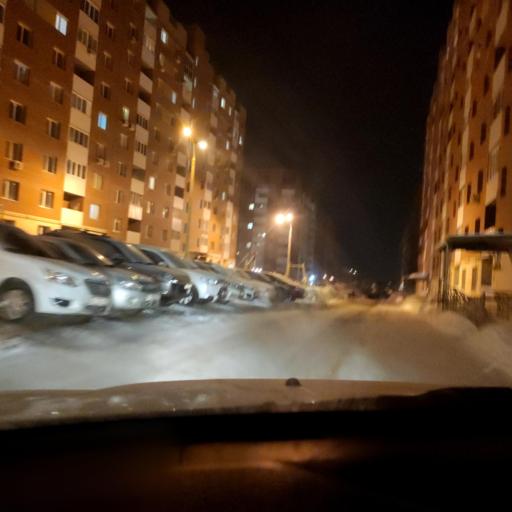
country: RU
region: Samara
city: Petra-Dubrava
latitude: 53.3070
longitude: 50.2874
